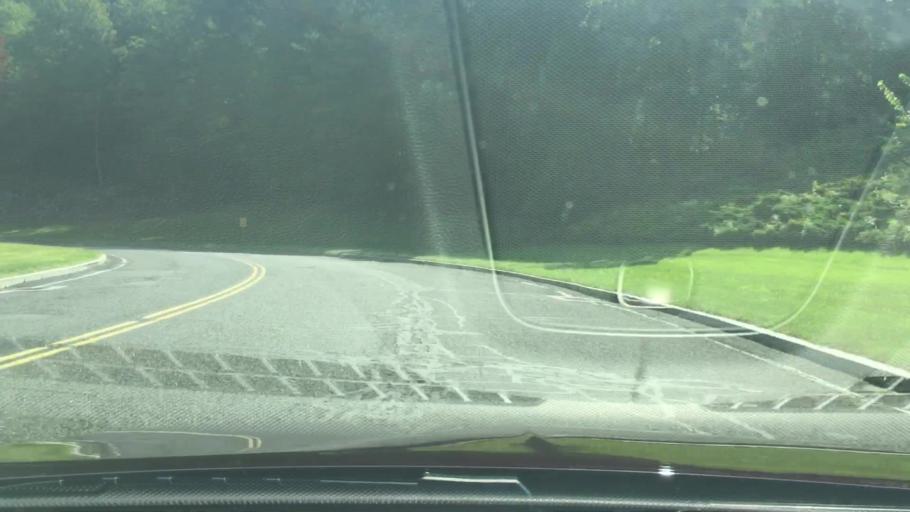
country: US
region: Connecticut
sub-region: Fairfield County
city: Danbury
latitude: 41.4260
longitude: -73.4108
